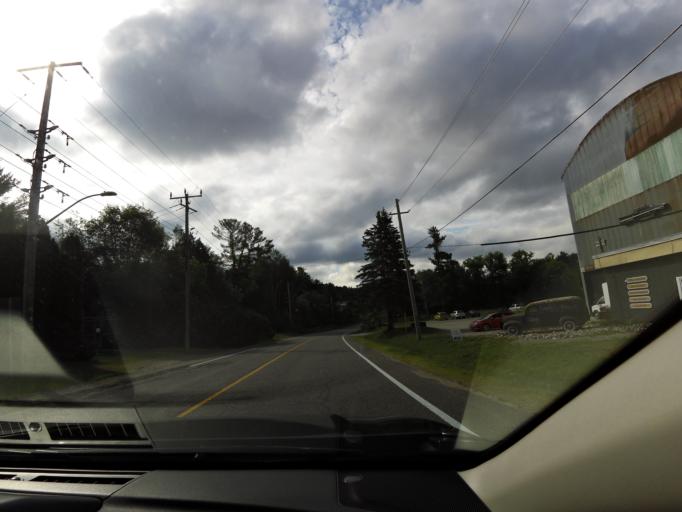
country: CA
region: Ontario
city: Bracebridge
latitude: 45.0363
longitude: -79.3051
